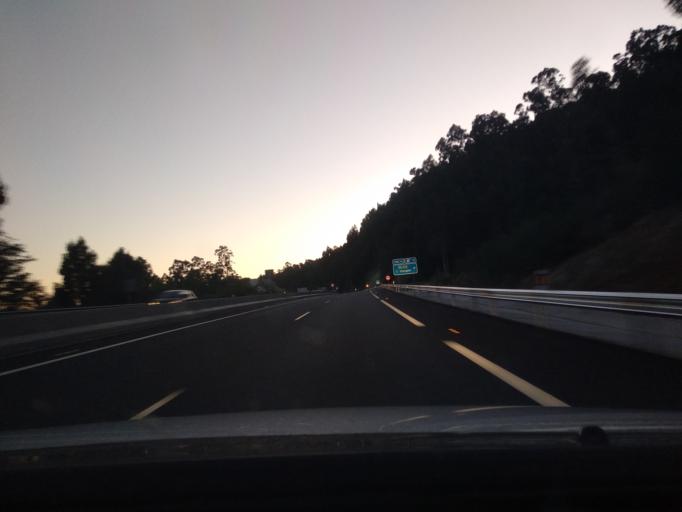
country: ES
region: Galicia
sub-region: Provincia de Pontevedra
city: Moana
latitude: 42.2967
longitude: -8.7483
